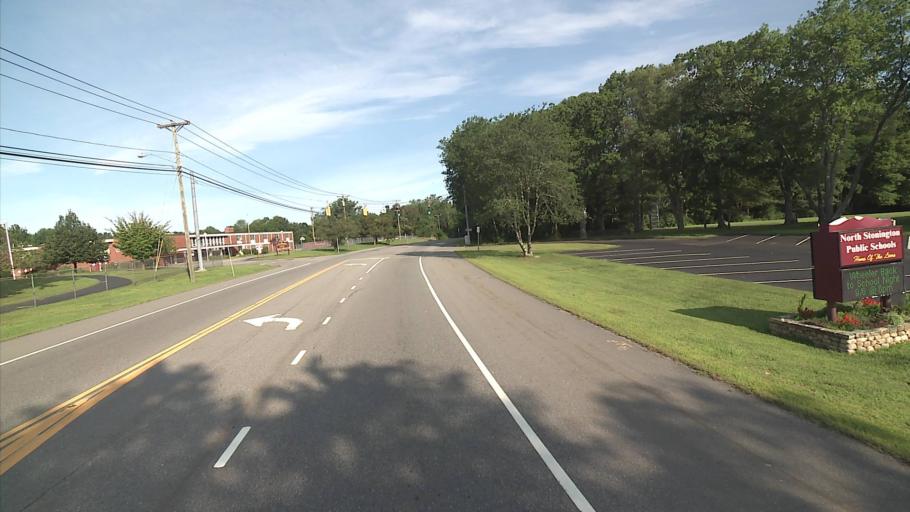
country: US
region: Connecticut
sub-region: New London County
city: Pawcatuck
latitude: 41.4395
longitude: -71.8873
